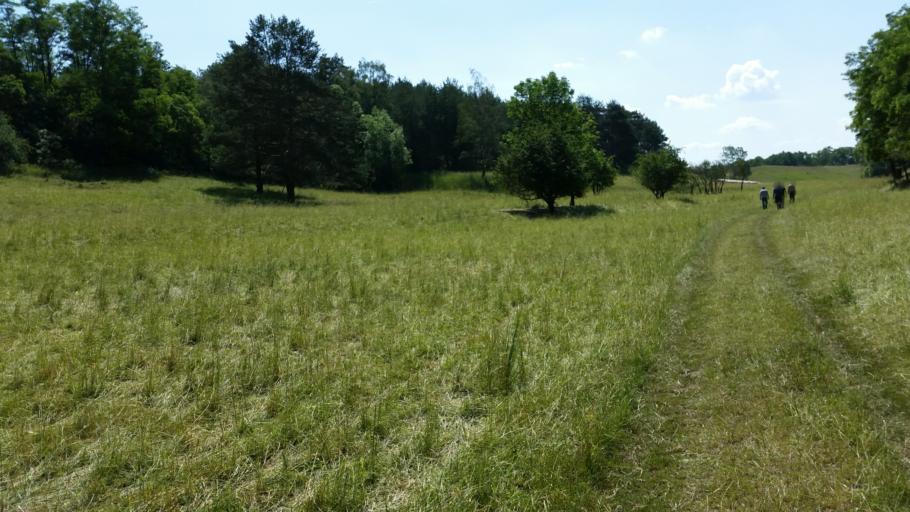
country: DE
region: Brandenburg
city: Podelzig
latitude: 52.4635
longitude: 14.4991
